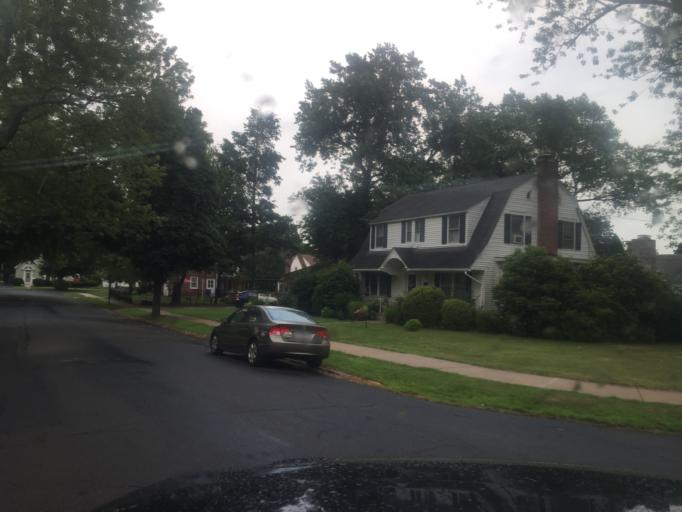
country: US
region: Connecticut
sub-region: Hartford County
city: New Britain
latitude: 41.6961
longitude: -72.7711
